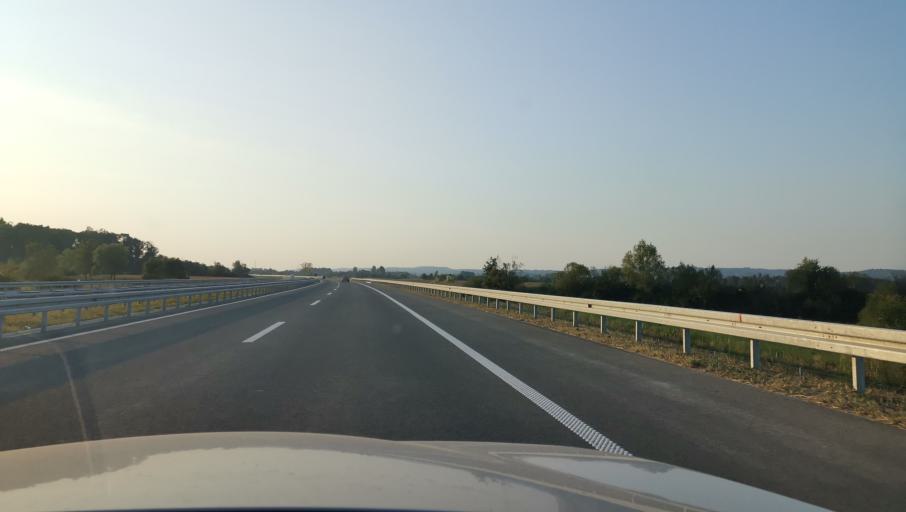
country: RS
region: Central Serbia
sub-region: Kolubarski Okrug
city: Ljig
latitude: 44.2743
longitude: 20.2661
